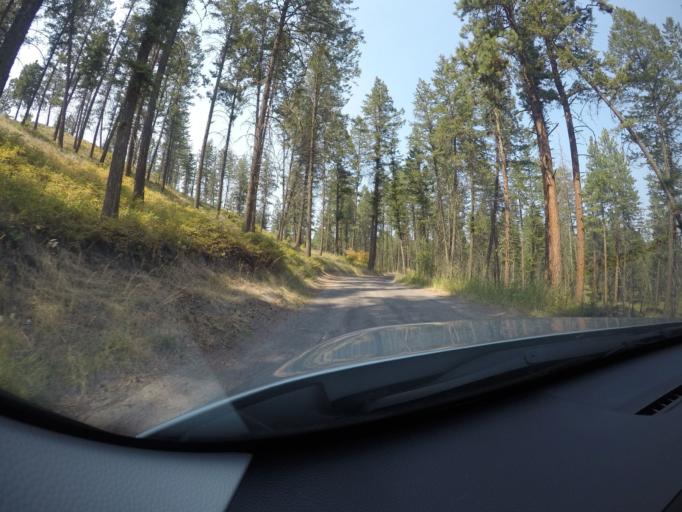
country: US
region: Montana
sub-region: Lake County
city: Polson
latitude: 47.7710
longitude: -114.1424
